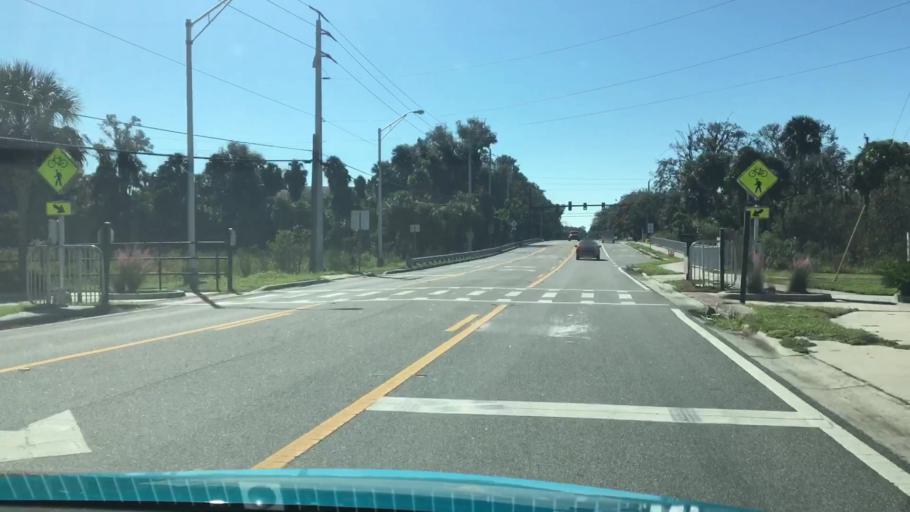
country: US
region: Florida
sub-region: Seminole County
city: Heathrow
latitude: 28.7941
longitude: -81.3630
